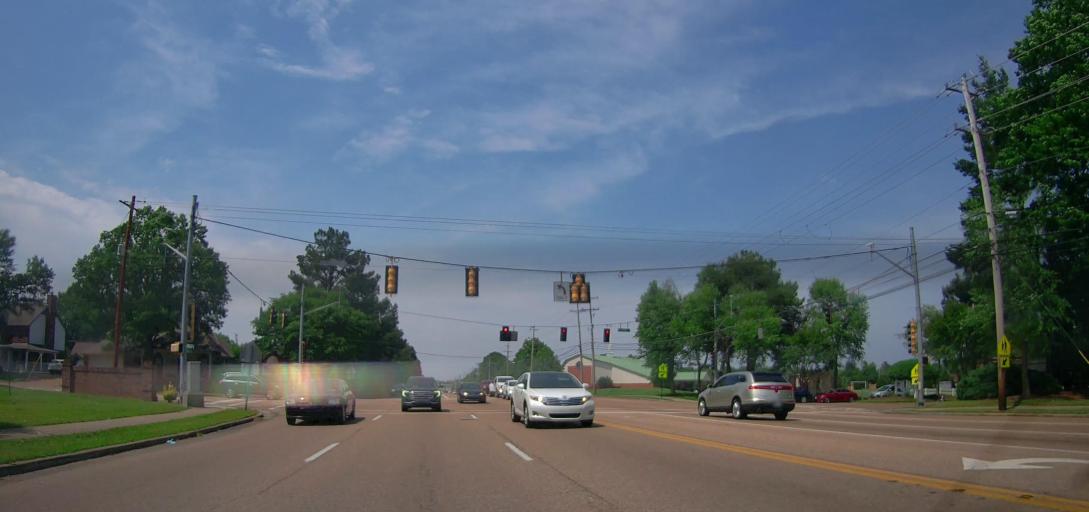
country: US
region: Tennessee
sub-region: Shelby County
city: Germantown
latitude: 35.0276
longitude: -89.7958
